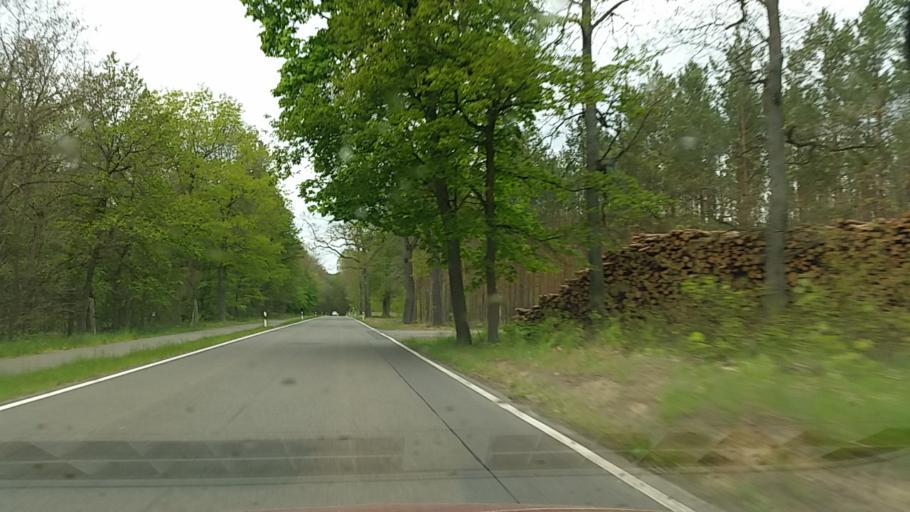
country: DE
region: Brandenburg
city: Reichenwalde
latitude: 52.3074
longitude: 13.9705
